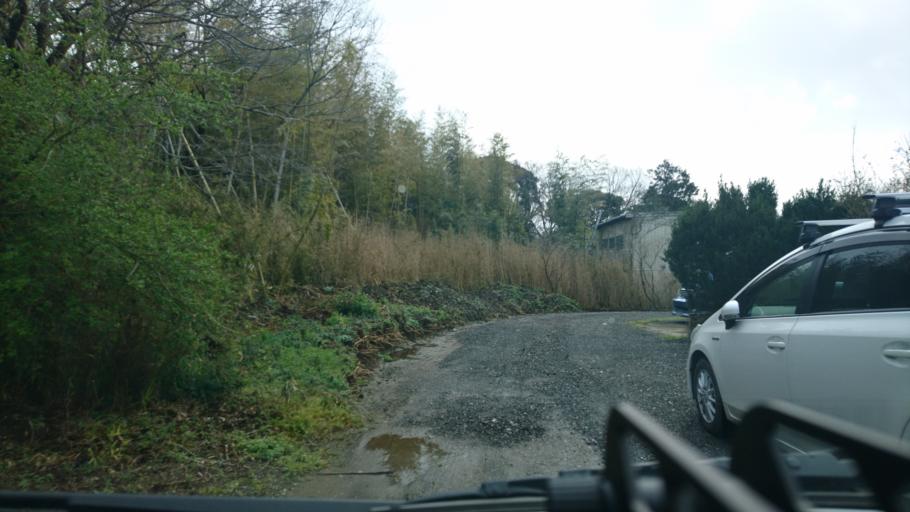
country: JP
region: Chiba
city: Kimitsu
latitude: 35.2940
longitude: 139.9670
